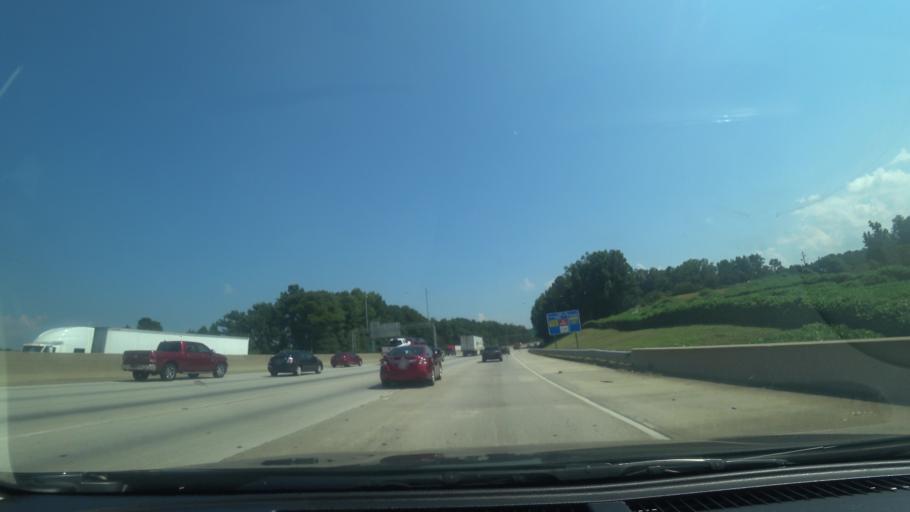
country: US
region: Georgia
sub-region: DeKalb County
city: Avondale Estates
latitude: 33.7739
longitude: -84.2358
